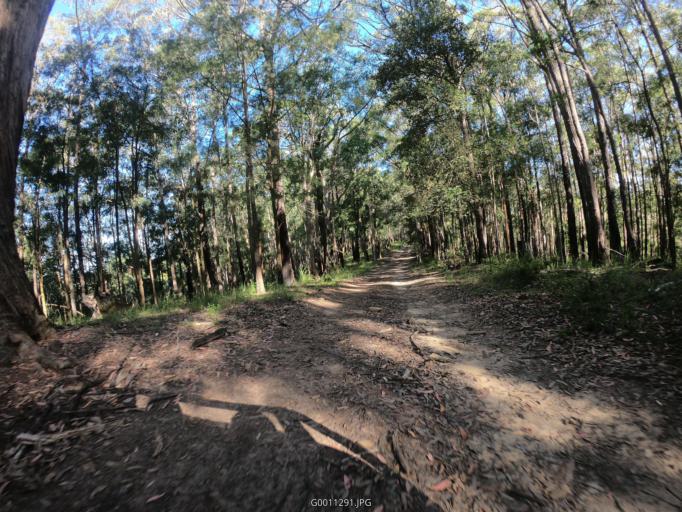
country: AU
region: New South Wales
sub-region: Lake Macquarie Shire
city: Cooranbong
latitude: -33.0223
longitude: 151.2979
